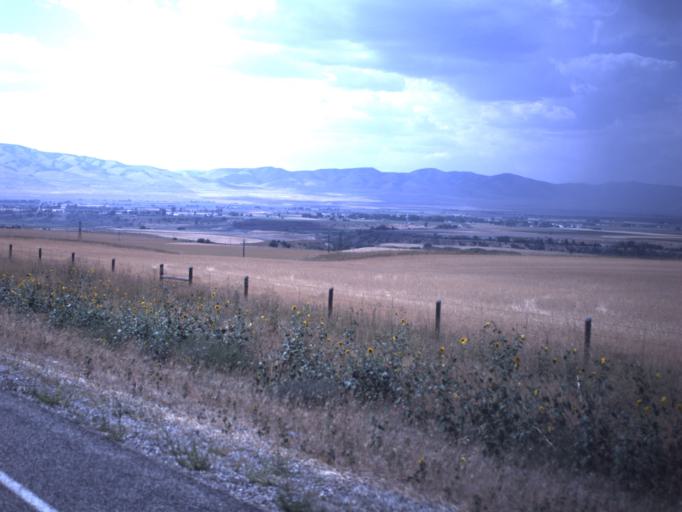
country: US
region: Utah
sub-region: Box Elder County
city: Garland
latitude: 41.7939
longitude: -112.0600
